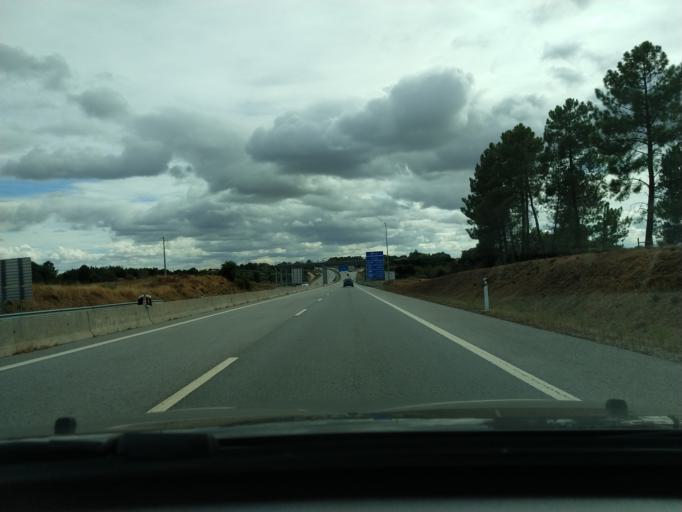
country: PT
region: Castelo Branco
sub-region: Concelho do Fundao
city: Fundao
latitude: 40.0347
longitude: -7.4689
